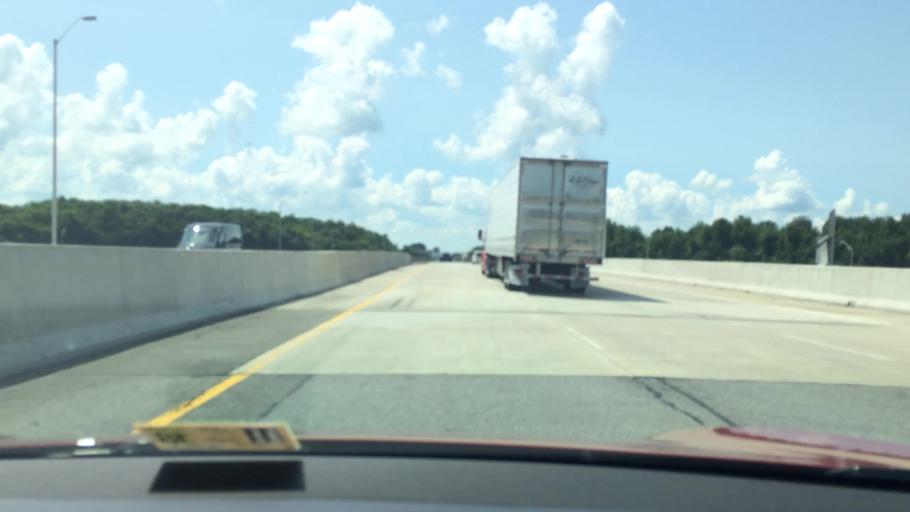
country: US
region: Indiana
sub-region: Saint Joseph County
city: South Bend
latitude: 41.7065
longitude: -86.3399
